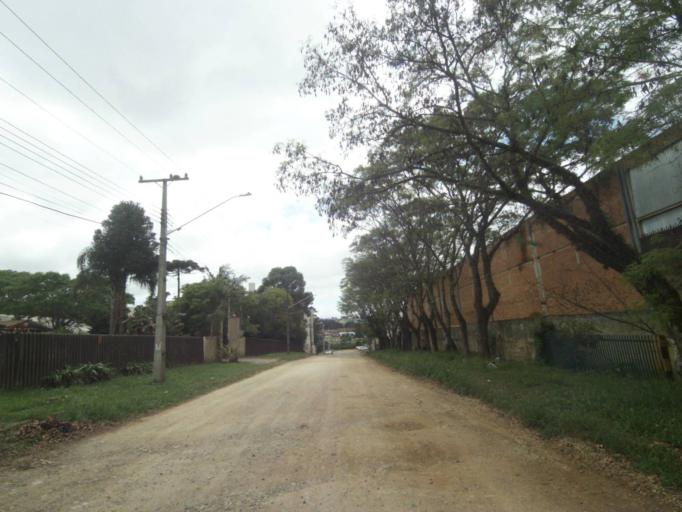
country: BR
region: Parana
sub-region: Pinhais
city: Pinhais
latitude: -25.4075
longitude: -49.2223
